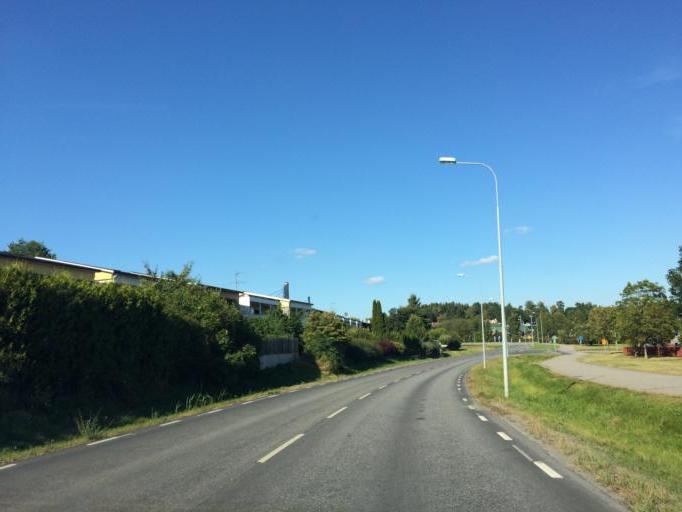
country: SE
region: Stockholm
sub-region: Upplands Vasby Kommun
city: Upplands Vaesby
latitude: 59.4945
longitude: 17.9492
